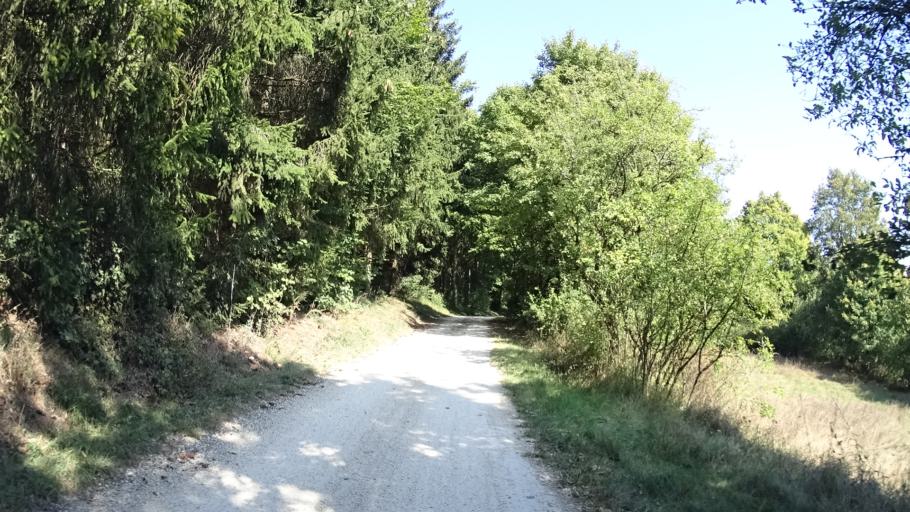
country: DE
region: Bavaria
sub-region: Upper Bavaria
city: Walting
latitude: 48.9480
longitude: 11.3568
